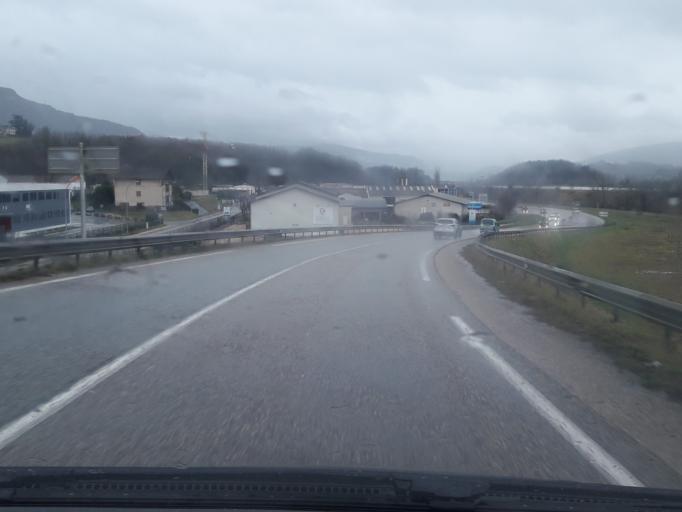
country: FR
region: Rhone-Alpes
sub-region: Departement de l'Ain
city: Belley
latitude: 45.7531
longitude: 5.7082
